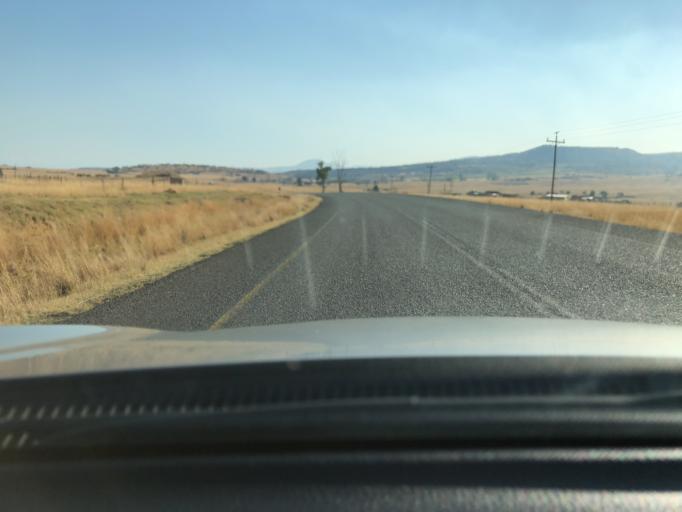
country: ZA
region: KwaZulu-Natal
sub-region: uThukela District Municipality
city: Ekuvukeni
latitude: -28.3337
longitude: 30.0506
